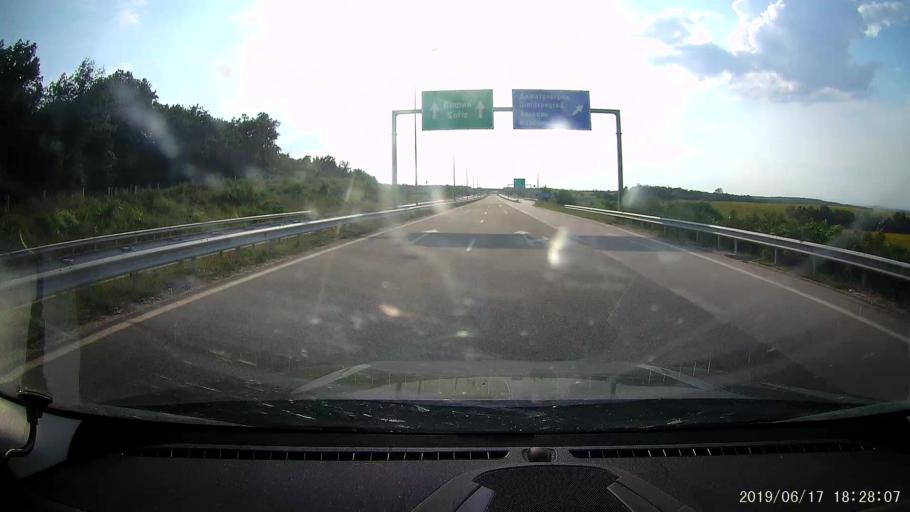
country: BG
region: Khaskovo
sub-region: Obshtina Dimitrovgrad
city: Dimitrovgrad
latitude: 42.0209
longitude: 25.5888
